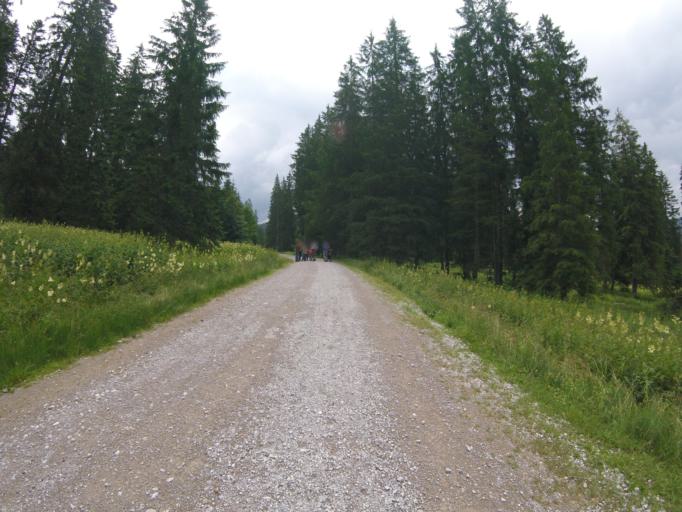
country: AT
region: Tyrol
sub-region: Politischer Bezirk Kitzbuhel
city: Waidring
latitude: 47.6550
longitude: 12.5948
